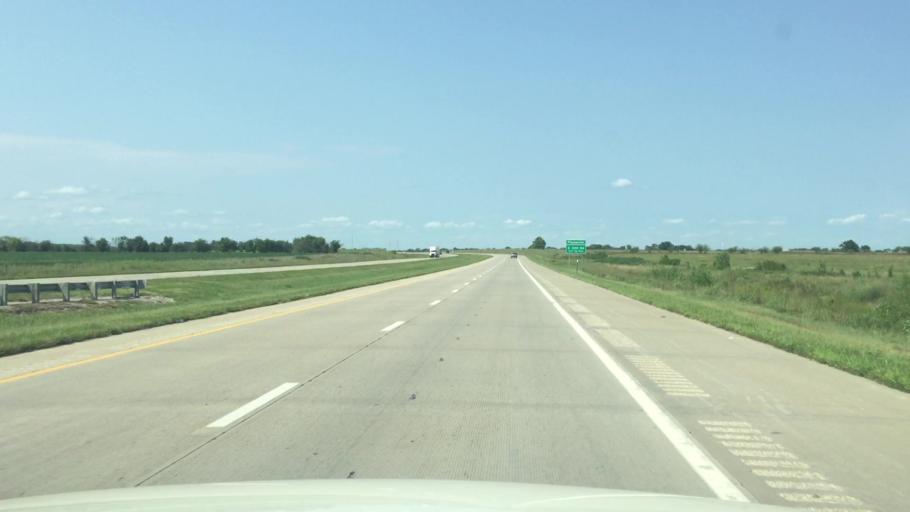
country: US
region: Kansas
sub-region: Linn County
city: Pleasanton
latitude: 38.1681
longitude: -94.6957
